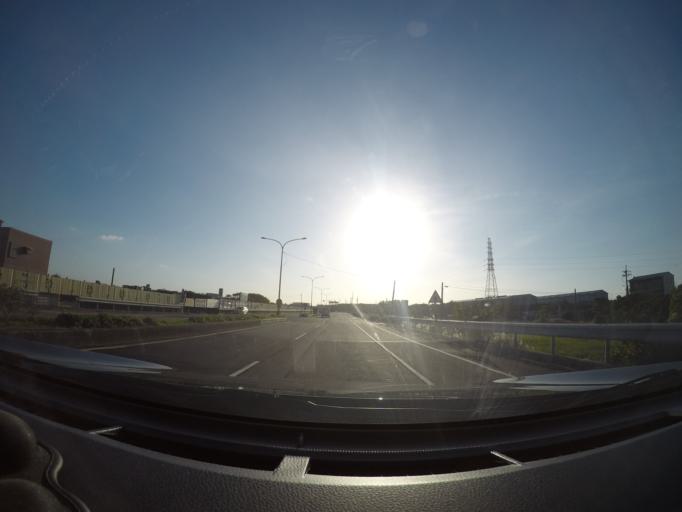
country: TW
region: Taiwan
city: Taoyuan City
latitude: 25.0741
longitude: 121.2011
